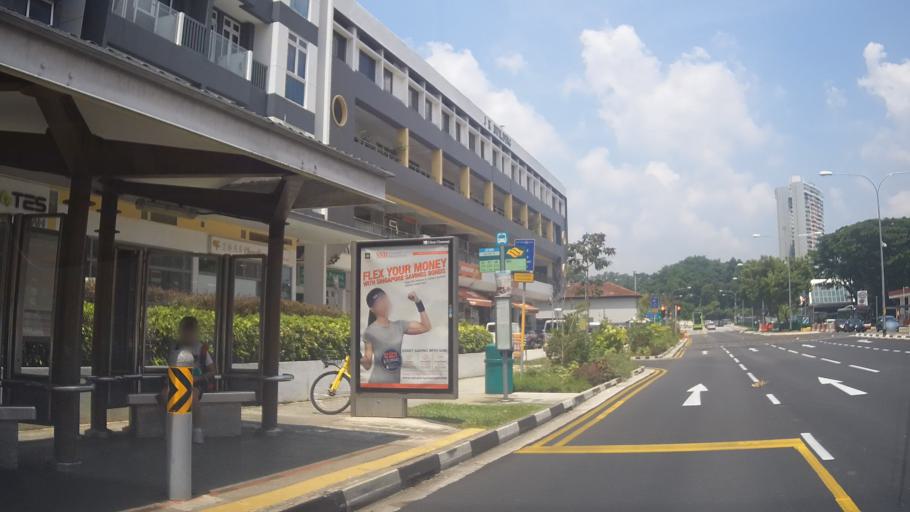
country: SG
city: Singapore
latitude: 1.3400
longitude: 103.7740
